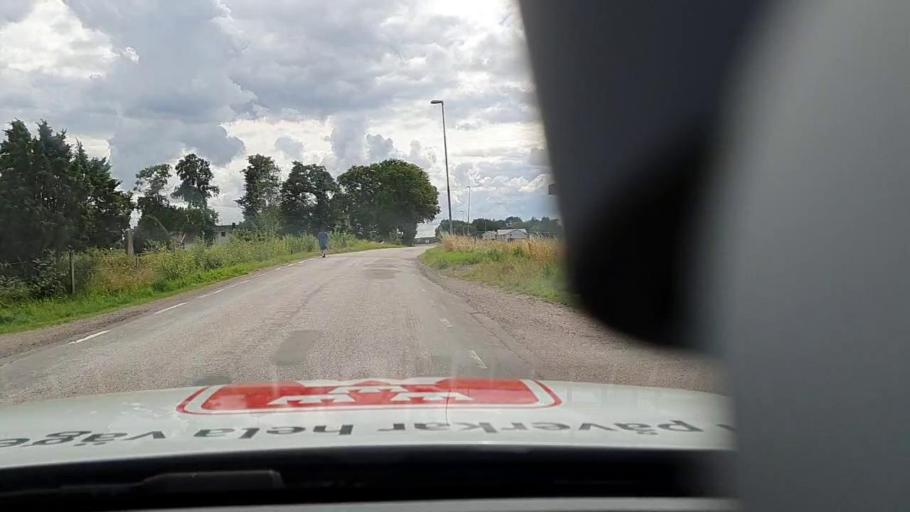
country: SE
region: Vaestra Goetaland
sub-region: Lidkopings Kommun
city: Lidkoping
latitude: 58.5584
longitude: 13.1160
